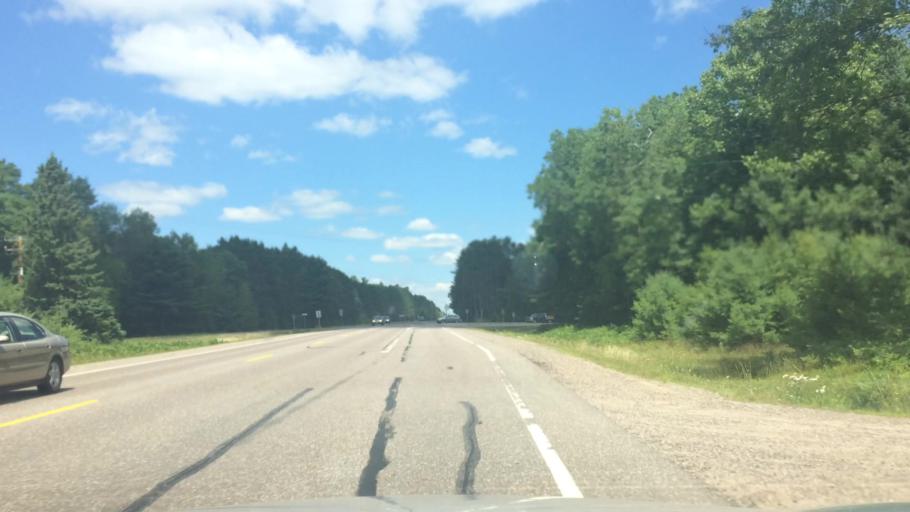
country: US
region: Wisconsin
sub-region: Vilas County
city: Lac du Flambeau
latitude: 45.9811
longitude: -89.6987
